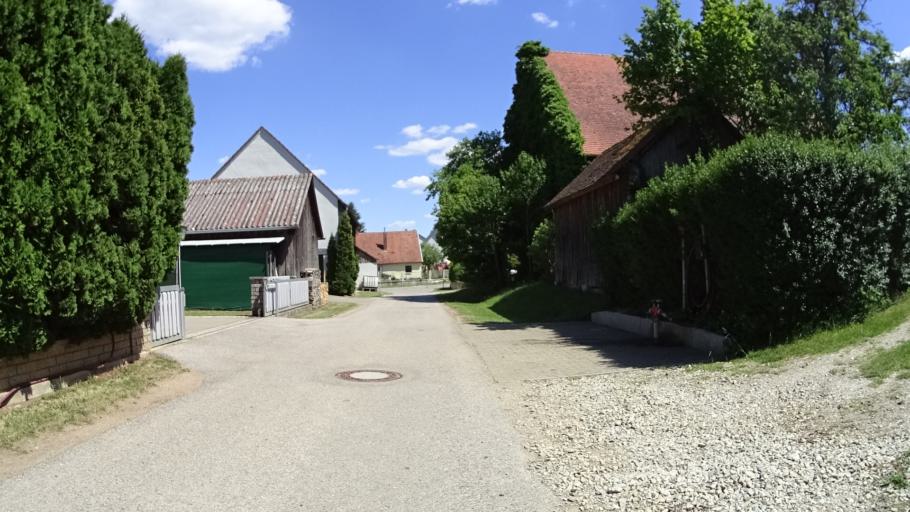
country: DE
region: Bavaria
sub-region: Regierungsbezirk Mittelfranken
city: Thalmassing
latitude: 49.0737
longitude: 11.2859
